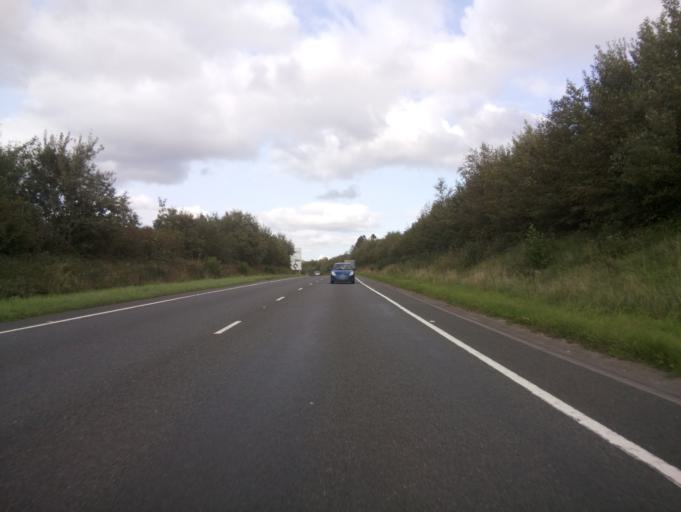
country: GB
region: Wales
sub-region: Rhondda Cynon Taf
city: Llantwit Fardre
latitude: 51.5562
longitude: -3.3194
